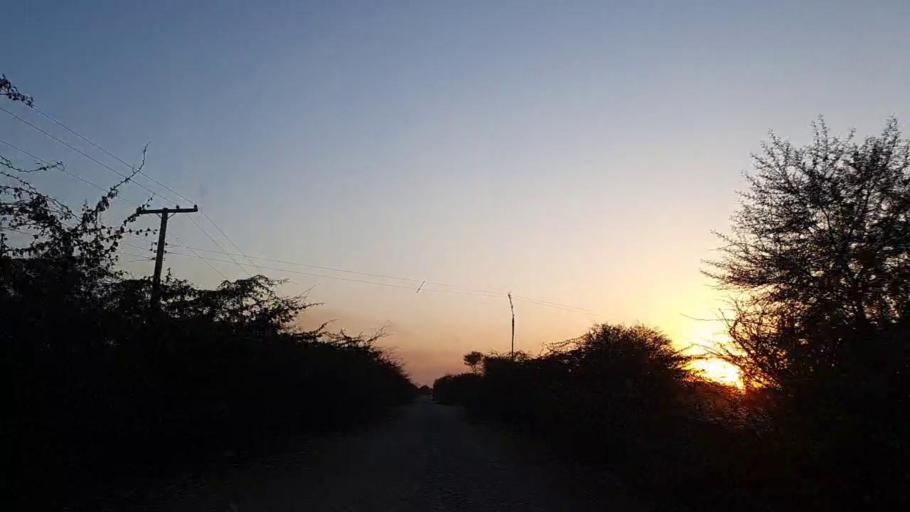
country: PK
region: Sindh
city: Daur
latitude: 26.3458
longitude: 68.3043
